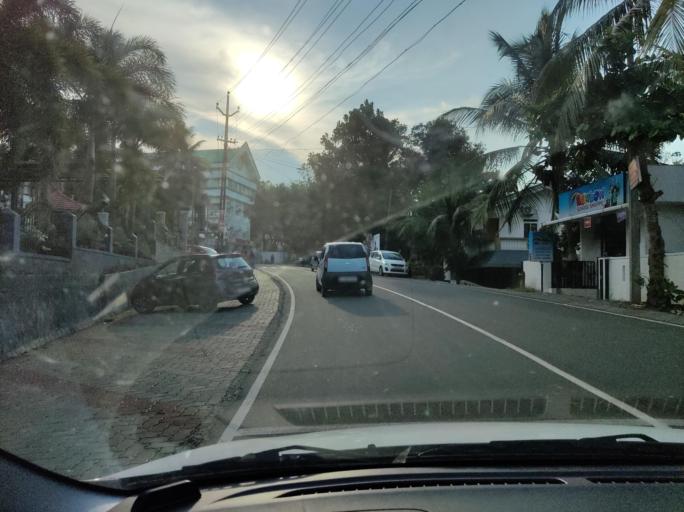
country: IN
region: Kerala
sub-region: Kottayam
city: Kottayam
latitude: 9.6481
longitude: 76.5235
